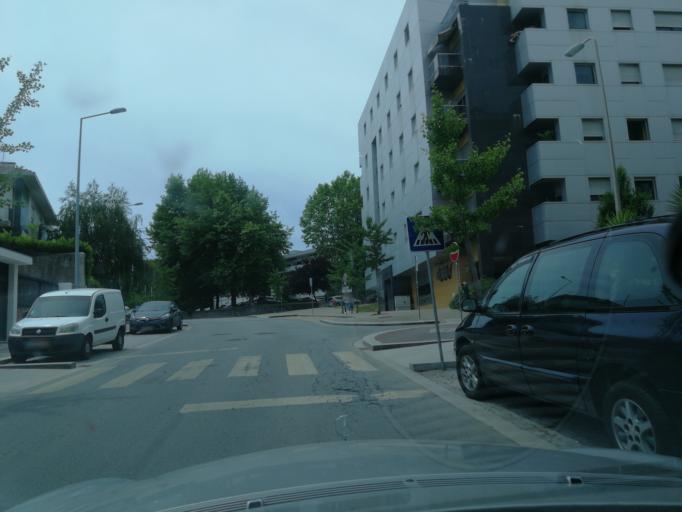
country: PT
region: Braga
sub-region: Vila Nova de Famalicao
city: Vila Nova de Famalicao
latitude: 41.4124
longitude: -8.5204
